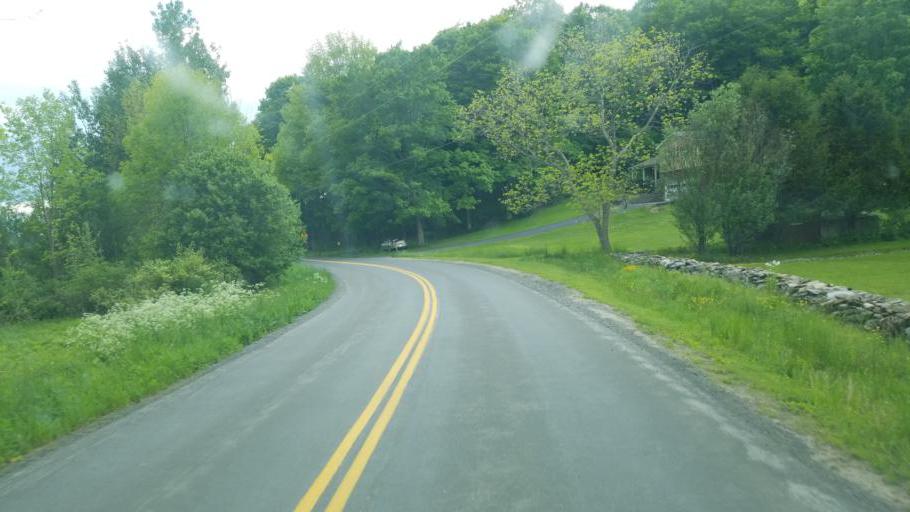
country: US
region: New York
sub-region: Herkimer County
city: Frankfort
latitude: 42.9225
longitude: -75.1356
